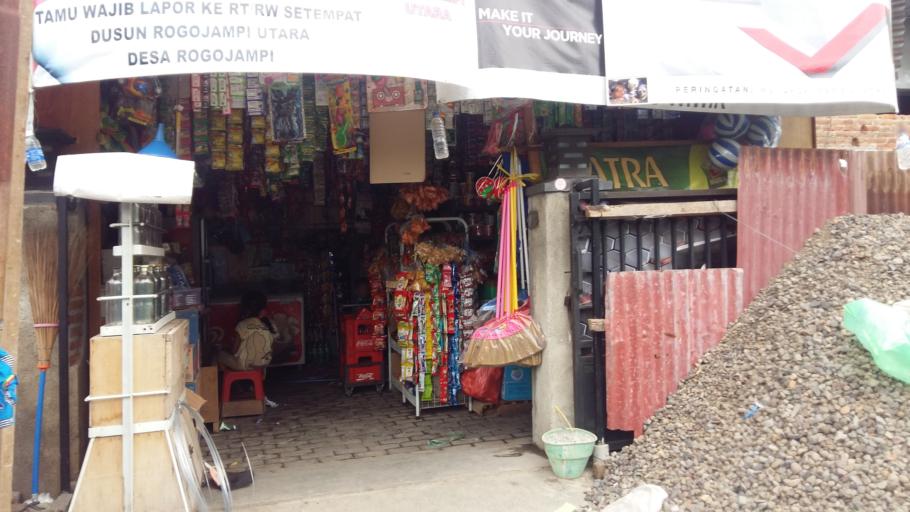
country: ID
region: East Java
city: Krajan
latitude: -8.3086
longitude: 114.2943
